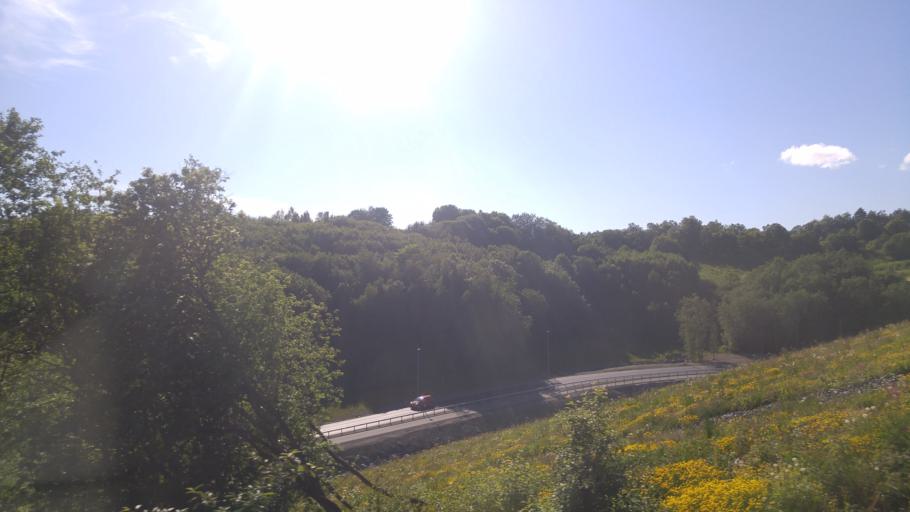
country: NO
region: Sor-Trondelag
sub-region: Melhus
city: Melhus
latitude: 63.3402
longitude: 10.3411
